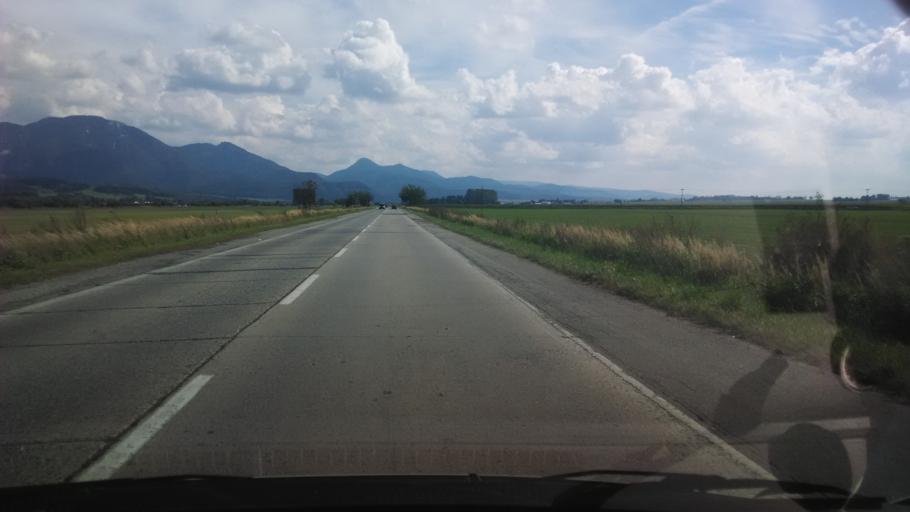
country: SK
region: Zilinsky
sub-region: Okres Martin
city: Martin
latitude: 48.9904
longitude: 18.8924
